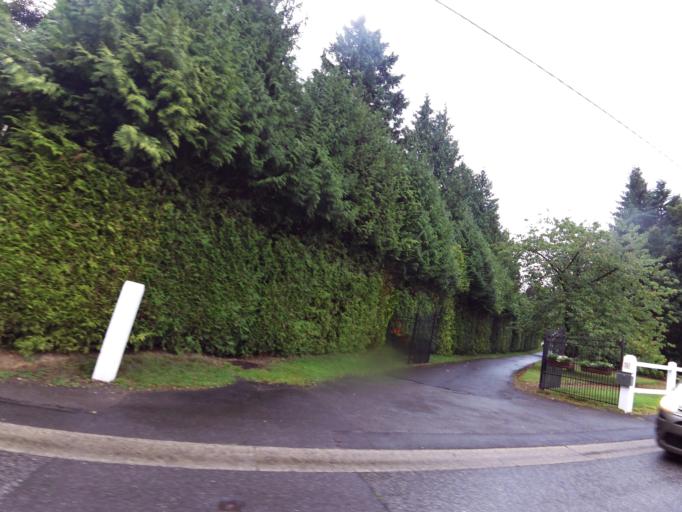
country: BE
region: Wallonia
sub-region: Province de Namur
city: Rochefort
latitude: 50.1547
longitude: 5.2257
